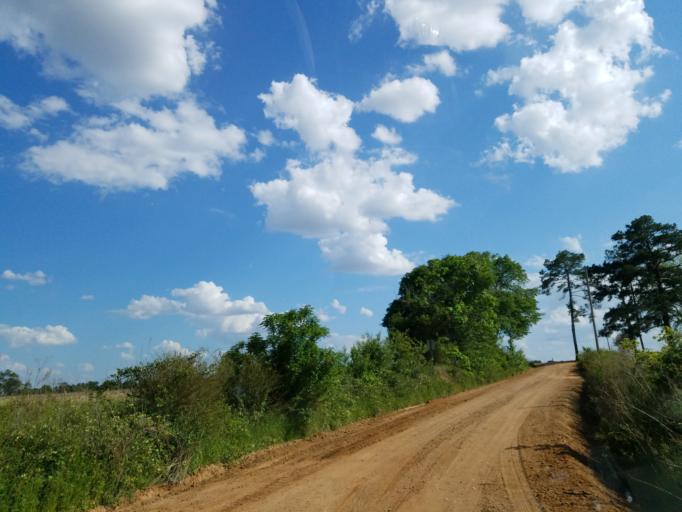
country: US
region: Georgia
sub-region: Crisp County
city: Cordele
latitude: 31.9956
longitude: -83.7408
